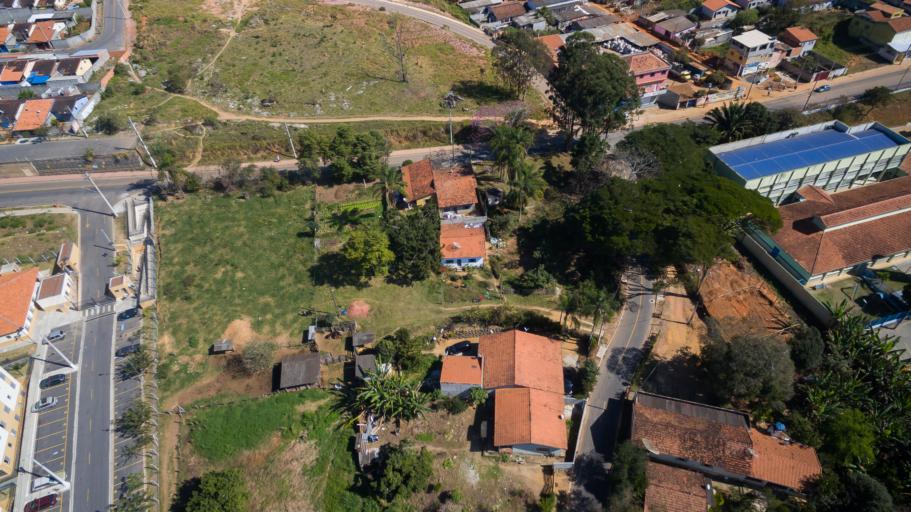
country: BR
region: Sao Paulo
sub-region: Sao Jose Dos Campos
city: Sao Jose dos Campos
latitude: -23.2229
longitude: -45.7926
